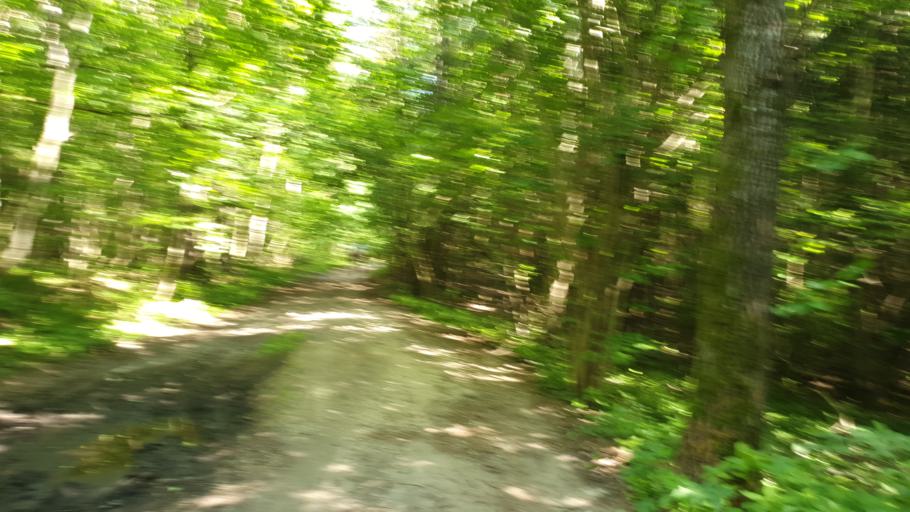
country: LT
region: Vilnius County
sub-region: Vilnius
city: Fabijoniskes
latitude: 54.7895
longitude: 25.3125
